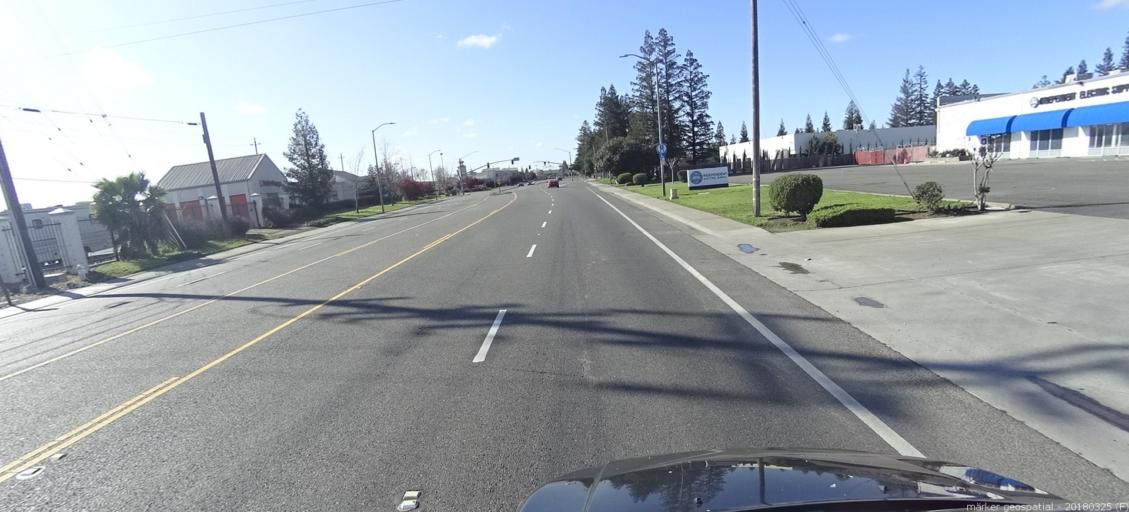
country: US
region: California
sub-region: Sacramento County
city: Rio Linda
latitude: 38.6488
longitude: -121.4755
